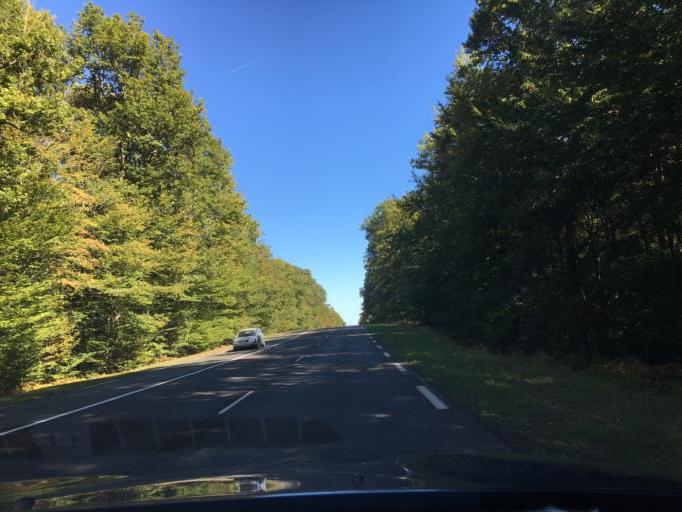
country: FR
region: Centre
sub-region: Departement d'Indre-et-Loire
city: Cheille
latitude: 47.2363
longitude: 0.4143
